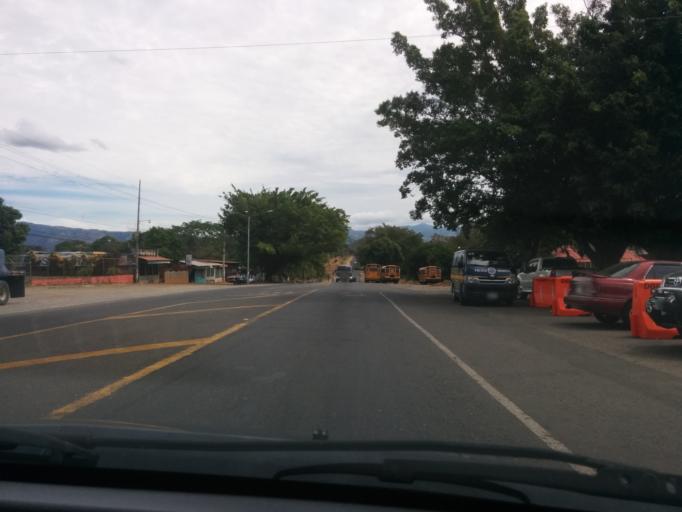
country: CR
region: Puntarenas
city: Esparza
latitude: 9.9976
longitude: -84.6563
